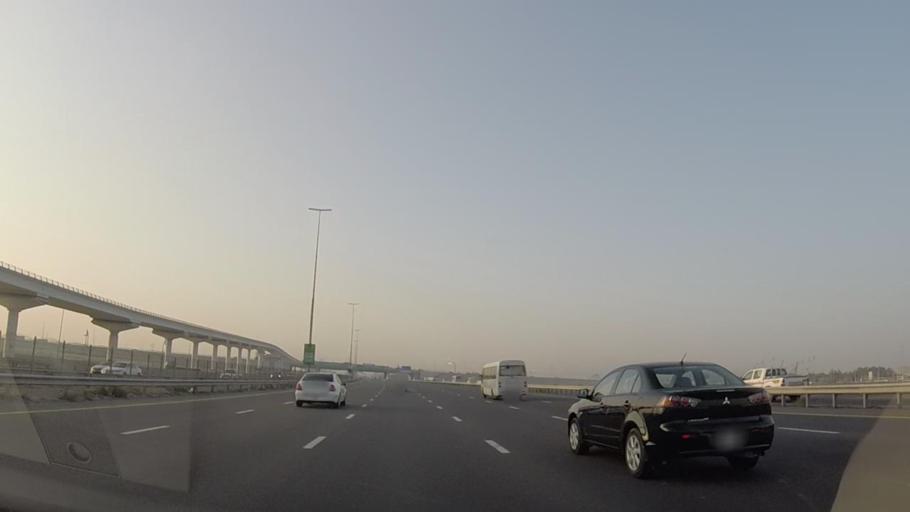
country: AE
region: Dubai
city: Dubai
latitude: 25.0209
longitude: 55.0985
